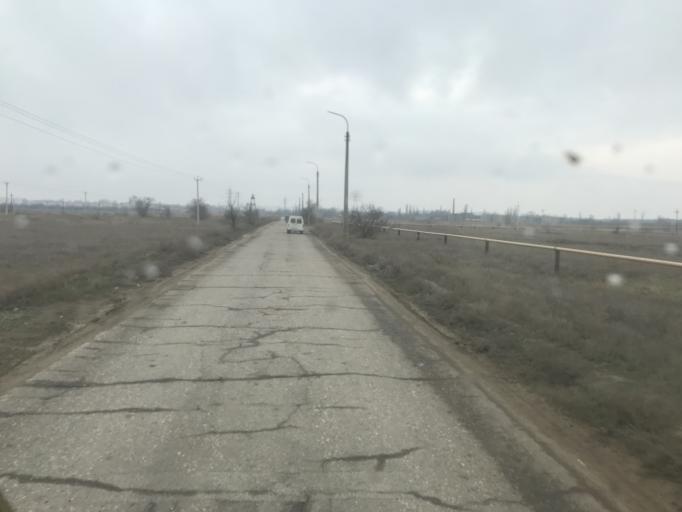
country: RU
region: Volgograd
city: Krasnoslobodsk
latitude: 48.5340
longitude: 44.6018
